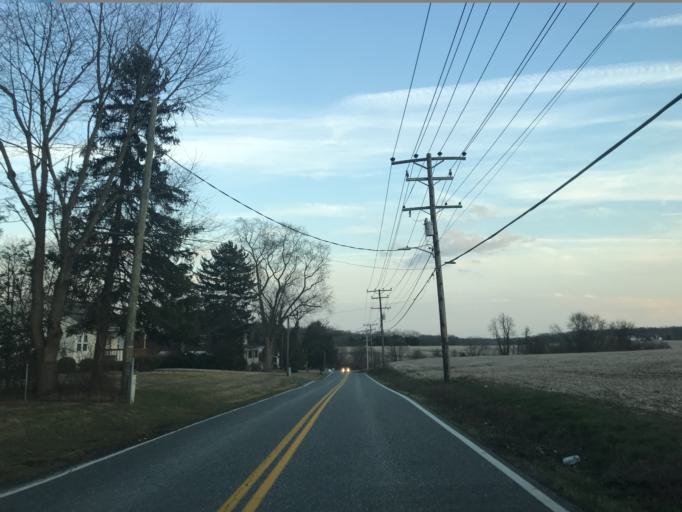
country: US
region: Maryland
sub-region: Harford County
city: Bel Air South
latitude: 39.5199
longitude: -76.2727
